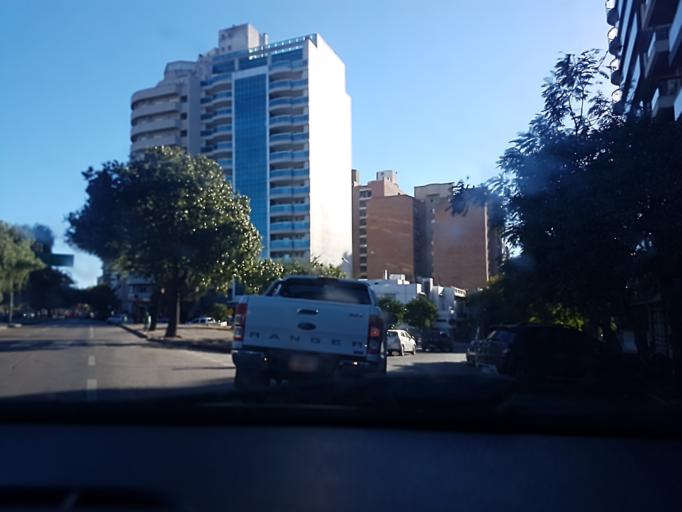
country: AR
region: Cordoba
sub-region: Departamento de Capital
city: Cordoba
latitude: -31.4274
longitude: -64.1822
